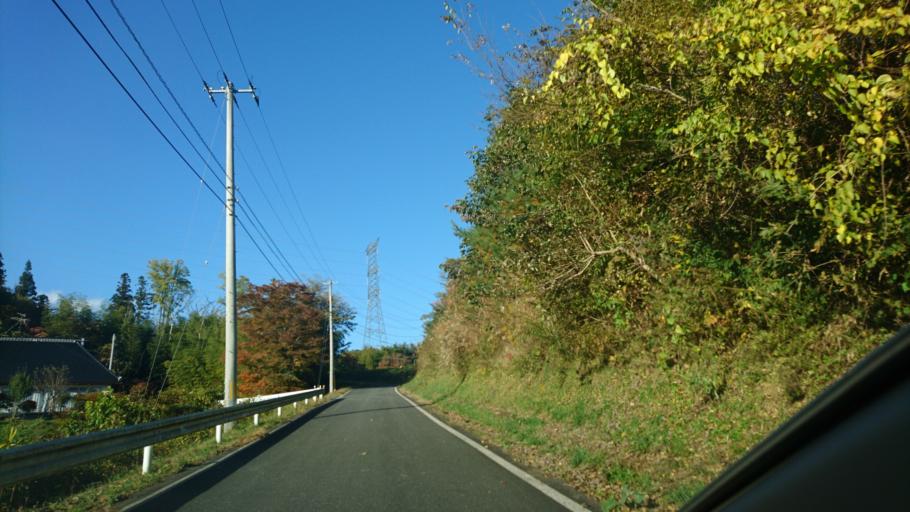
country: JP
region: Iwate
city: Ichinoseki
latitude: 38.9206
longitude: 141.2247
